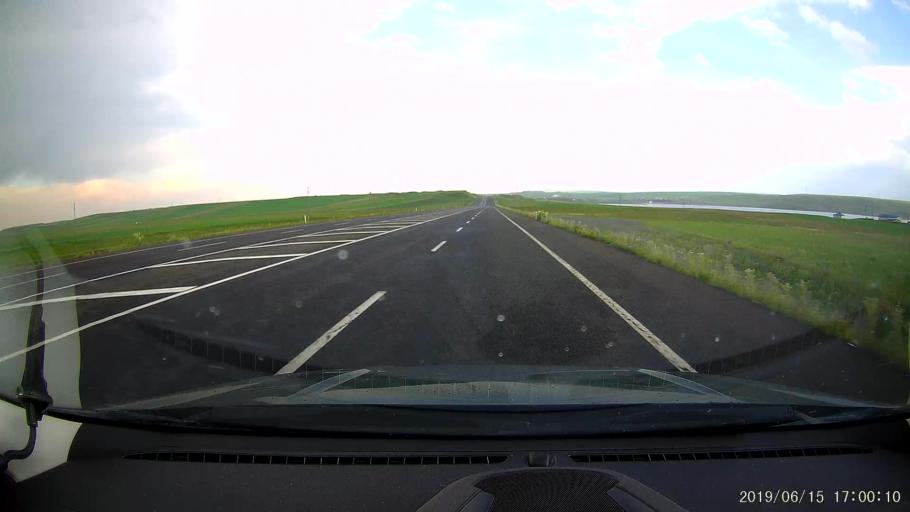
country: TR
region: Kars
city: Susuz
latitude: 40.7424
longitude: 43.1589
